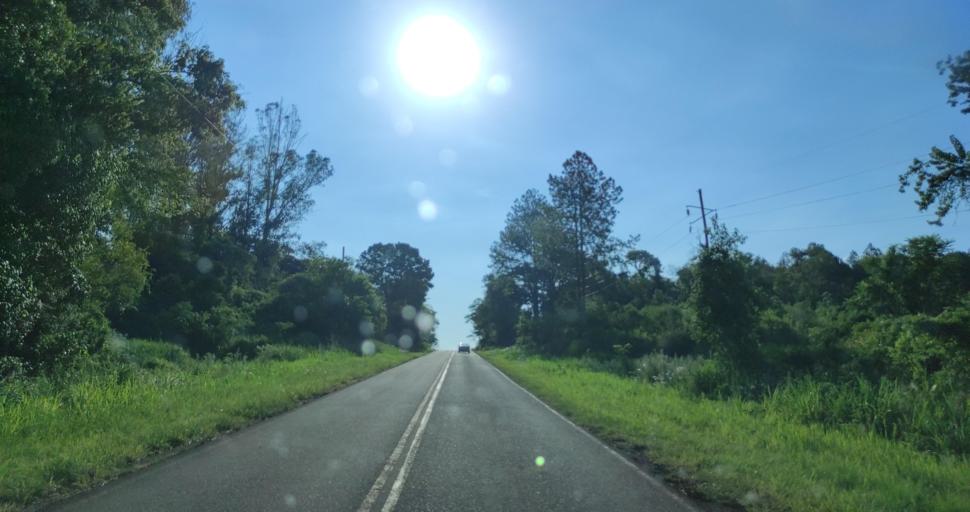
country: AR
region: Misiones
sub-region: Departamento de Eldorado
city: Eldorado
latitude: -26.3995
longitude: -54.3762
